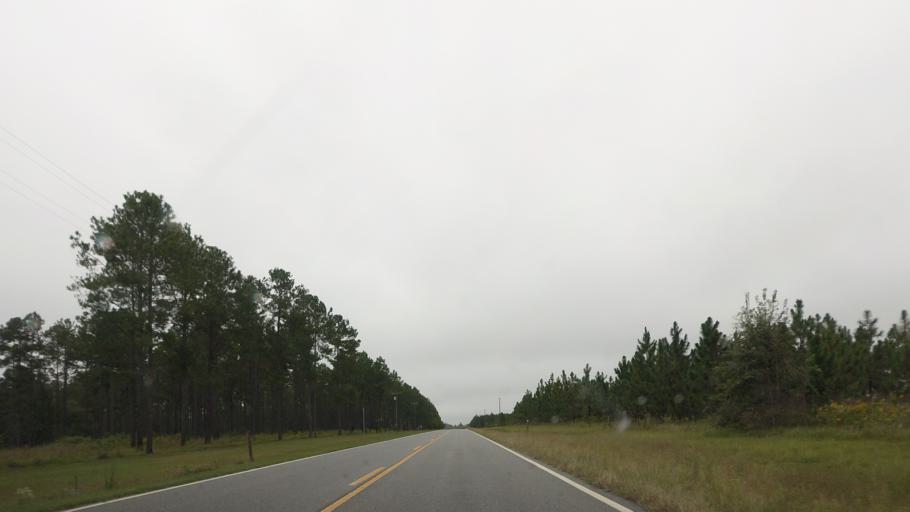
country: US
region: Georgia
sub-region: Berrien County
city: Enigma
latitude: 31.4428
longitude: -83.2402
